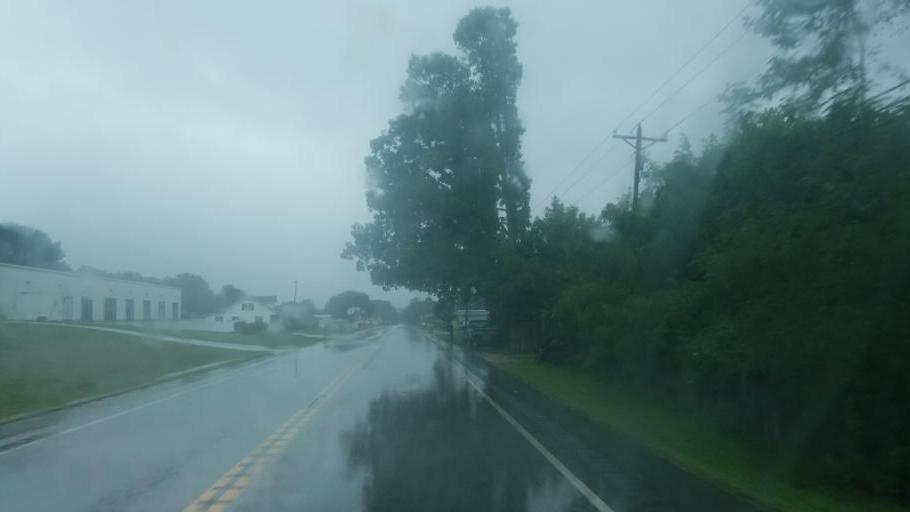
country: US
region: Kentucky
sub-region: Rowan County
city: Morehead
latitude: 38.2319
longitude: -83.4991
